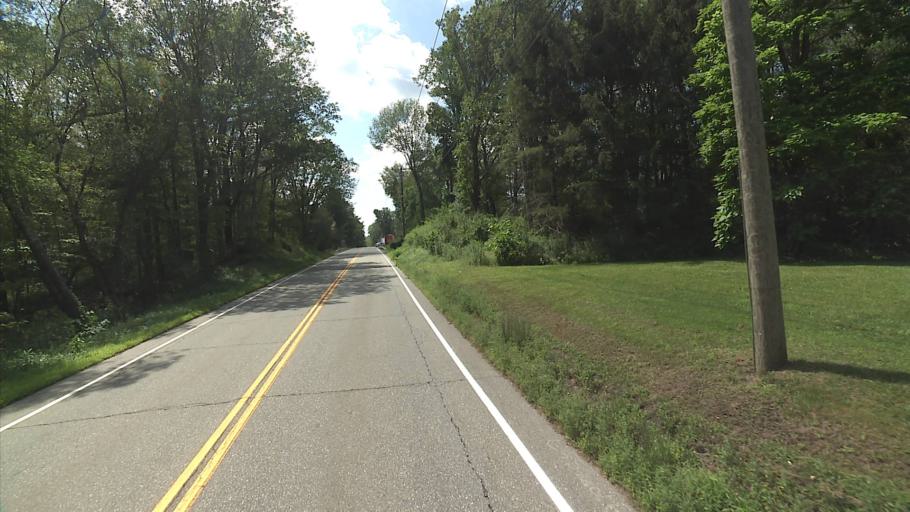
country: US
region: Connecticut
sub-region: Windham County
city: South Woodstock
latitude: 41.8753
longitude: -72.0873
